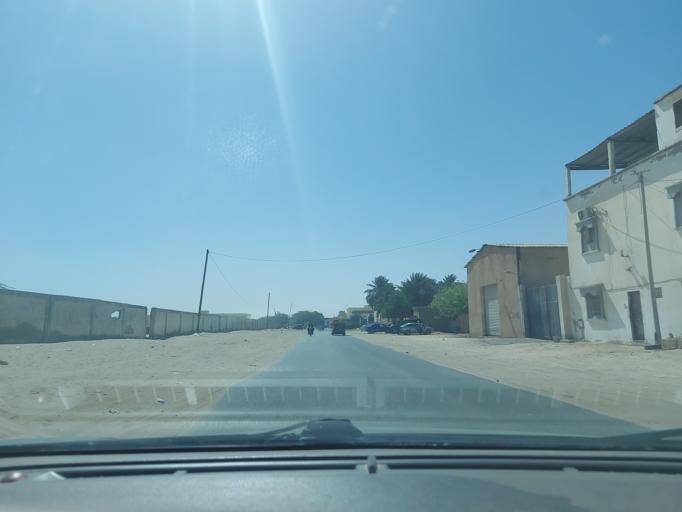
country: MR
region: Nouakchott
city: Nouakchott
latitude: 18.0614
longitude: -15.9753
